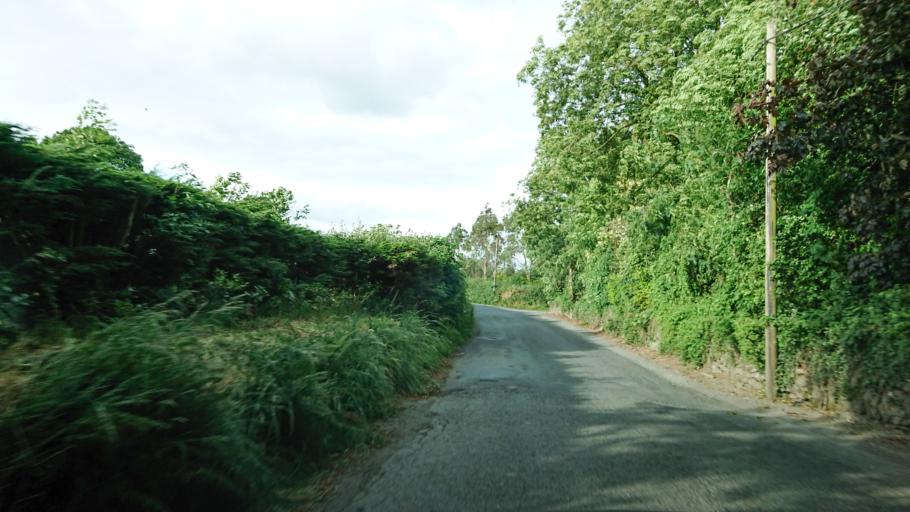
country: IE
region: Munster
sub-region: Waterford
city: Waterford
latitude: 52.2331
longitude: -7.1593
